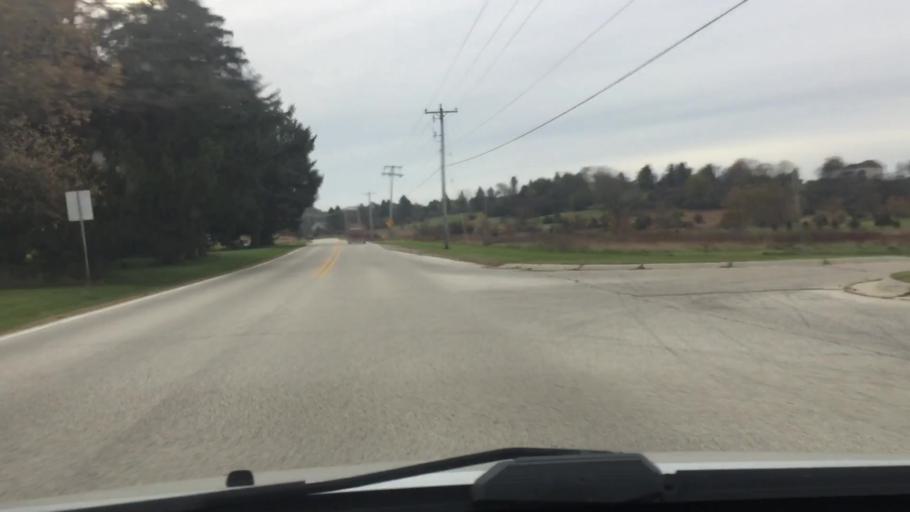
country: US
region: Wisconsin
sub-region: Waukesha County
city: Mukwonago
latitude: 42.8869
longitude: -88.3763
